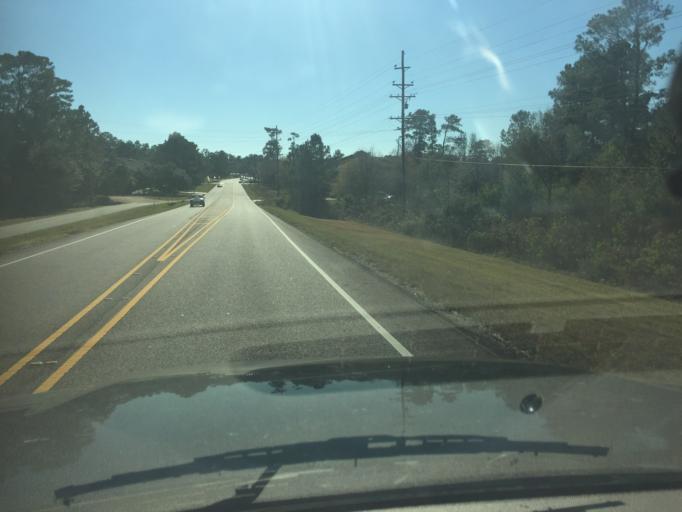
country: US
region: Louisiana
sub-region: Saint Tammany Parish
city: Slidell
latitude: 30.3001
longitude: -89.7235
